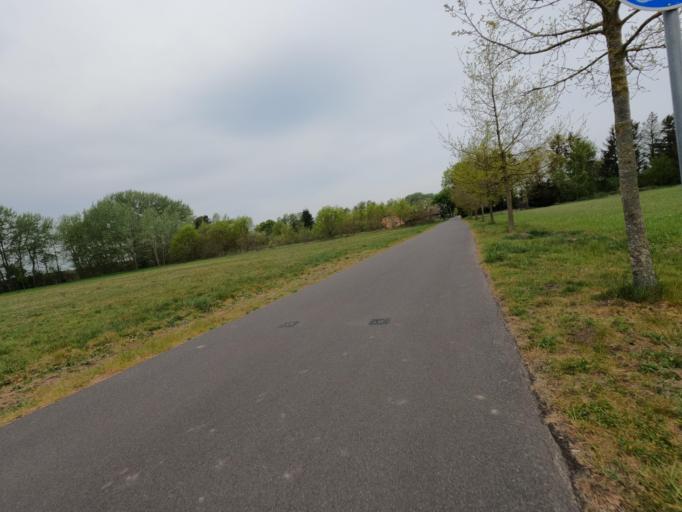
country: DE
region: Mecklenburg-Vorpommern
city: Zingst
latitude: 54.3727
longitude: 12.6384
